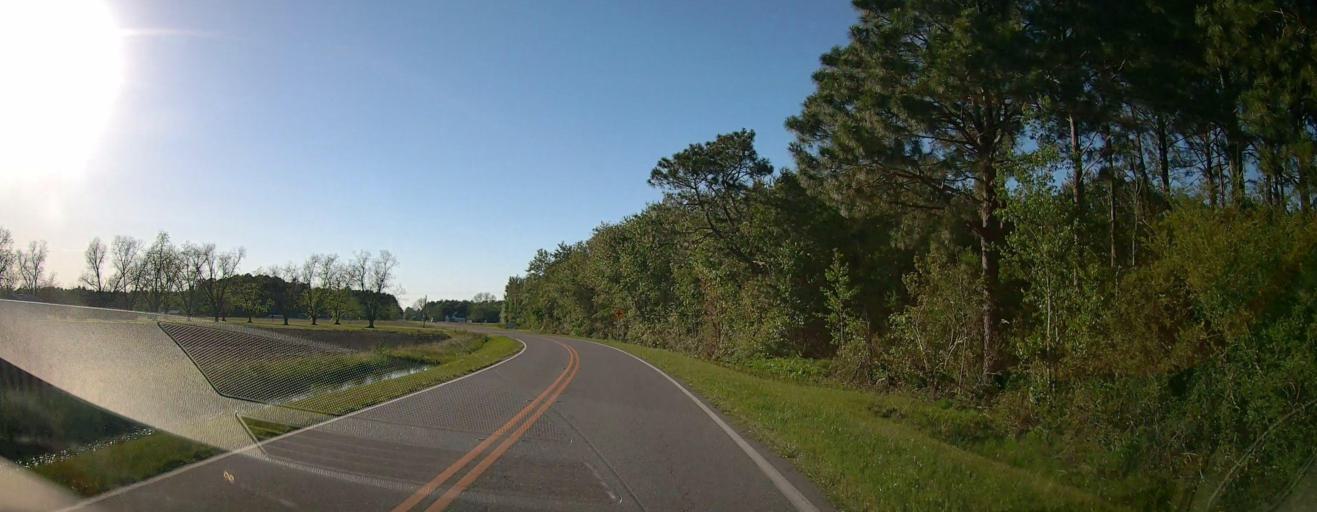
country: US
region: Georgia
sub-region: Ben Hill County
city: Fitzgerald
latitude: 31.6770
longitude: -83.1934
